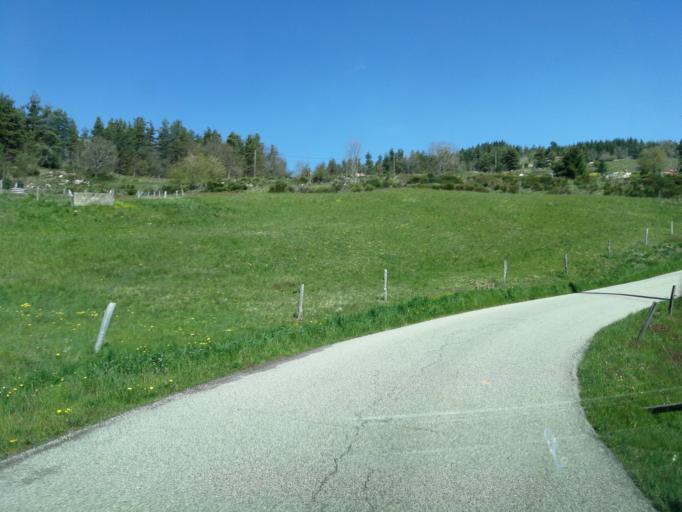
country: FR
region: Rhone-Alpes
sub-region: Departement de l'Ardeche
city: Le Cheylard
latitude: 44.9339
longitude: 4.4225
